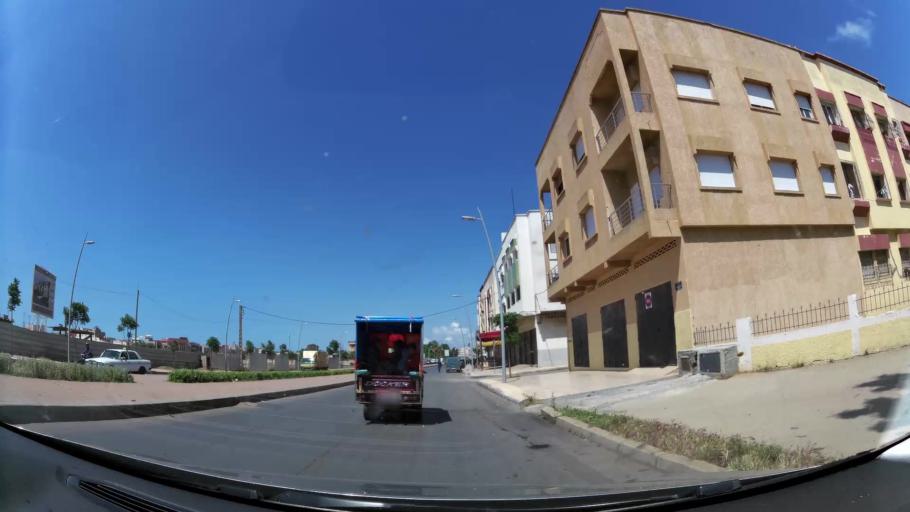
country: MA
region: Rabat-Sale-Zemmour-Zaer
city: Sale
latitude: 34.0473
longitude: -6.7881
